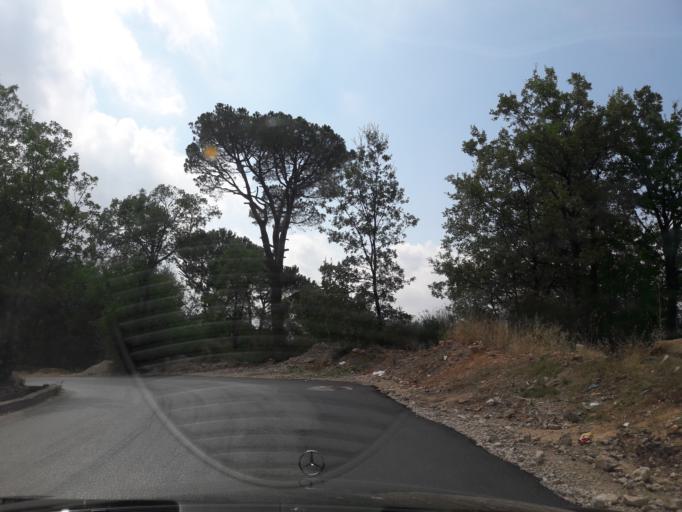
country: LB
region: Mont-Liban
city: Djounie
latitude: 33.9513
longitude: 35.7774
